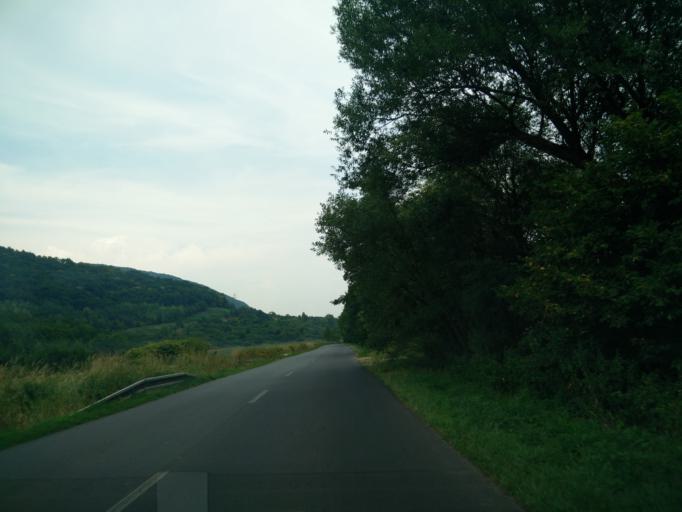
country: SK
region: Banskobystricky
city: Ziar nad Hronom
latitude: 48.5916
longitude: 18.8814
